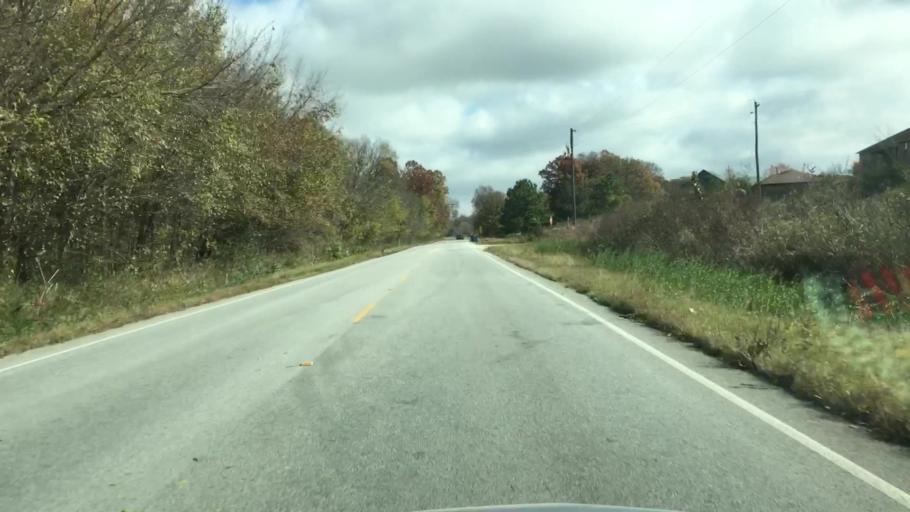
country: US
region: Arkansas
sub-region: Benton County
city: Gentry
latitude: 36.2579
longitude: -94.3874
